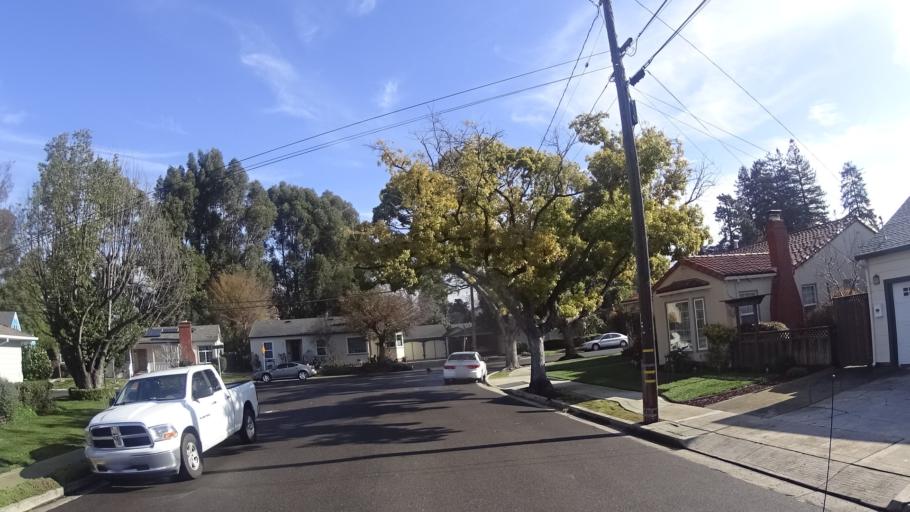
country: US
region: California
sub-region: Alameda County
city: Hayward
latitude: 37.6801
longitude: -122.0736
